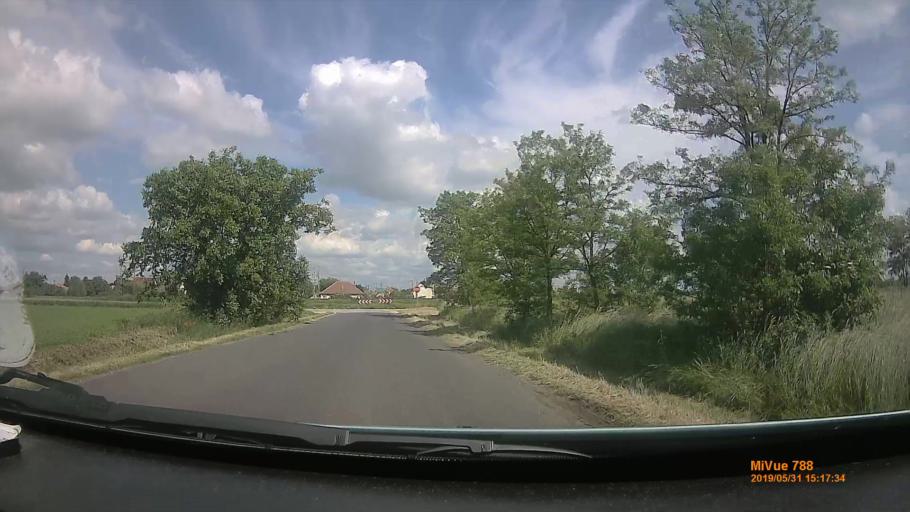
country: HU
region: Borsod-Abauj-Zemplen
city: Taktaharkany
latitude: 48.0829
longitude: 21.1219
